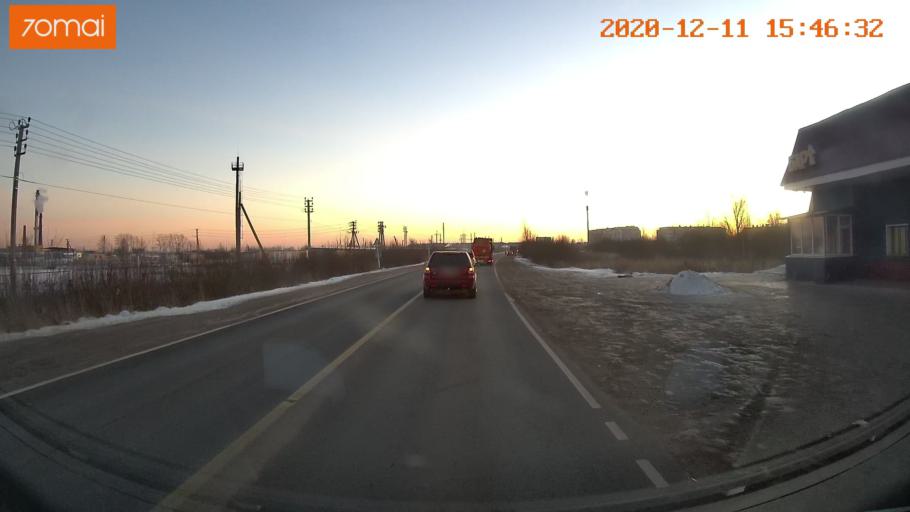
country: RU
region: Ivanovo
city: Novo-Talitsy
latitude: 57.0052
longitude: 40.8548
